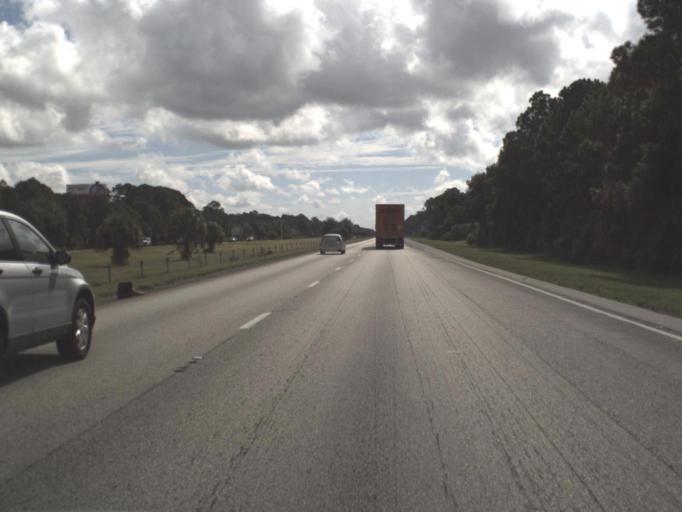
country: US
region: Florida
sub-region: Sarasota County
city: North Port
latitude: 27.0990
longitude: -82.1965
